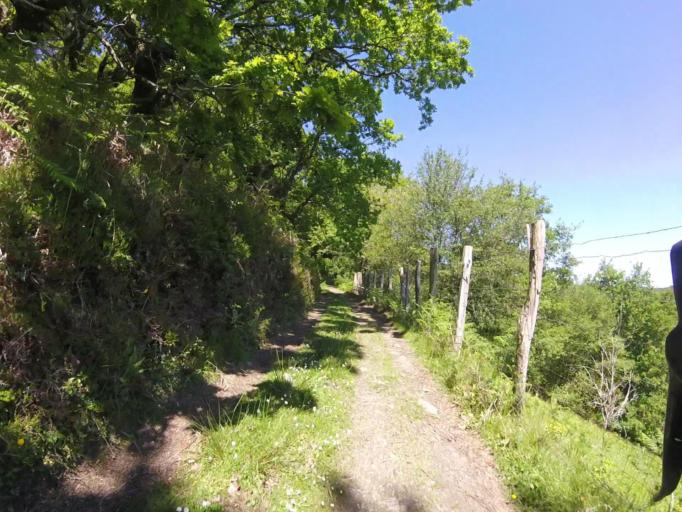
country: ES
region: Navarre
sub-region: Provincia de Navarra
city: Lesaka
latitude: 43.2453
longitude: -1.7496
